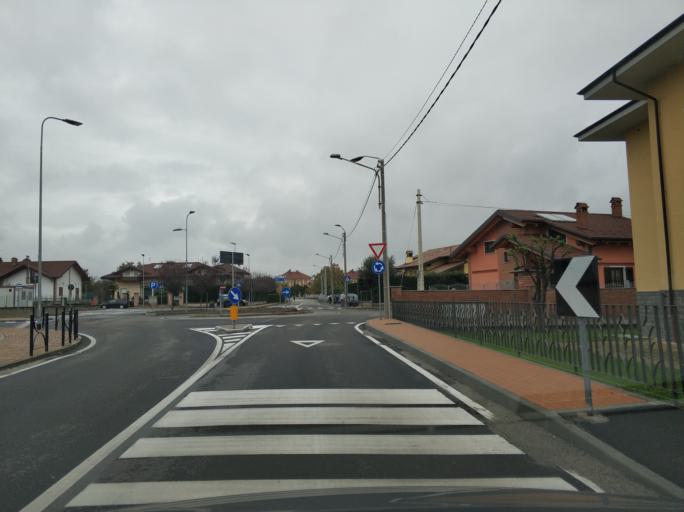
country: IT
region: Piedmont
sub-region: Provincia di Torino
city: Villanova Canavese
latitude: 45.2449
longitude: 7.5552
